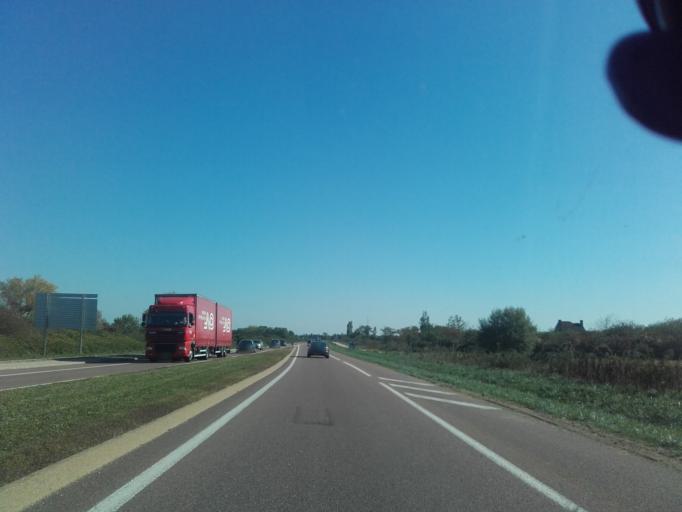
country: FR
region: Bourgogne
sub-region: Departement de la Cote-d'Or
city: Beaune
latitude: 47.0120
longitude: 4.8156
